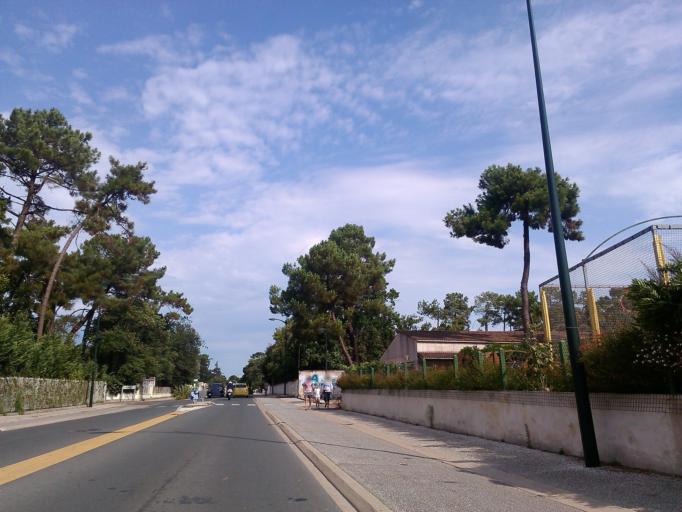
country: FR
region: Poitou-Charentes
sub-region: Departement de la Charente-Maritime
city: La Tremblade
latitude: 45.7889
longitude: -1.1588
